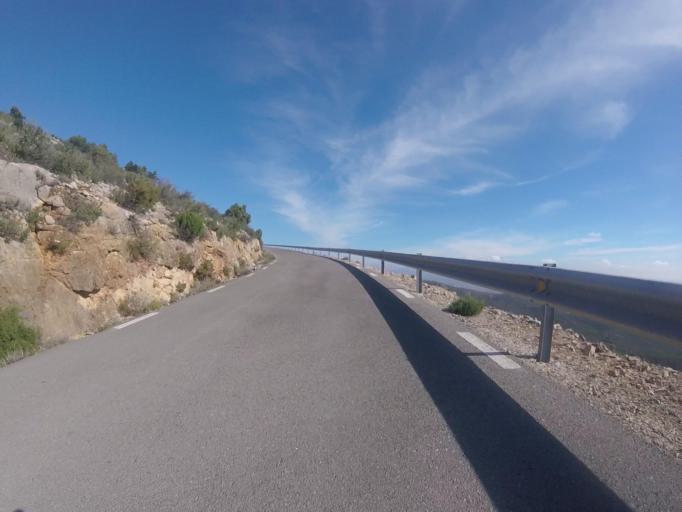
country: ES
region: Valencia
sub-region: Provincia de Castello
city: Sarratella
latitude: 40.2863
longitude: 0.0403
